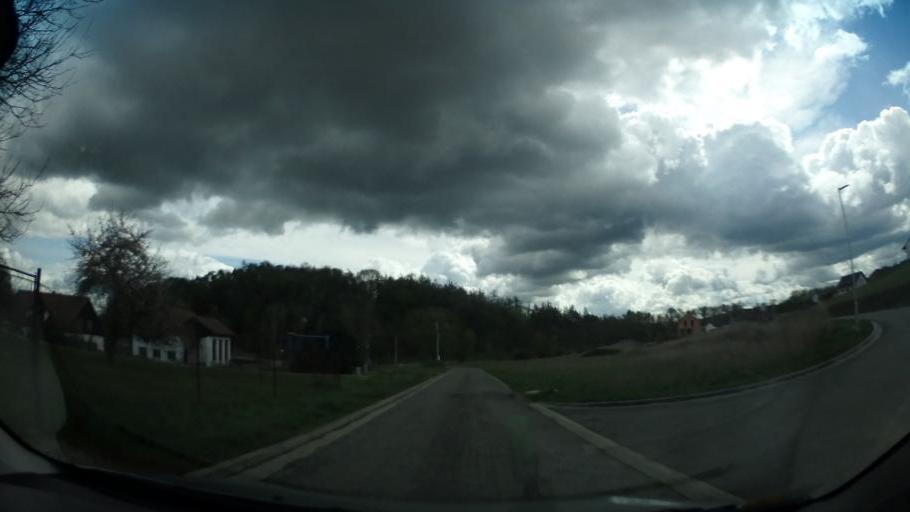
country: CZ
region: Vysocina
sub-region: Okres Zd'ar nad Sazavou
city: Velka Bites
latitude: 49.2931
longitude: 16.2323
